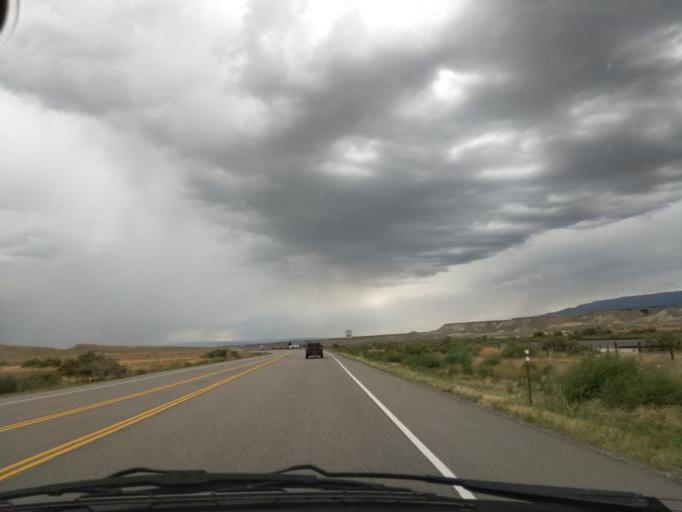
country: US
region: Colorado
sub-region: Delta County
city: Orchard City
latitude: 38.8007
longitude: -107.9058
